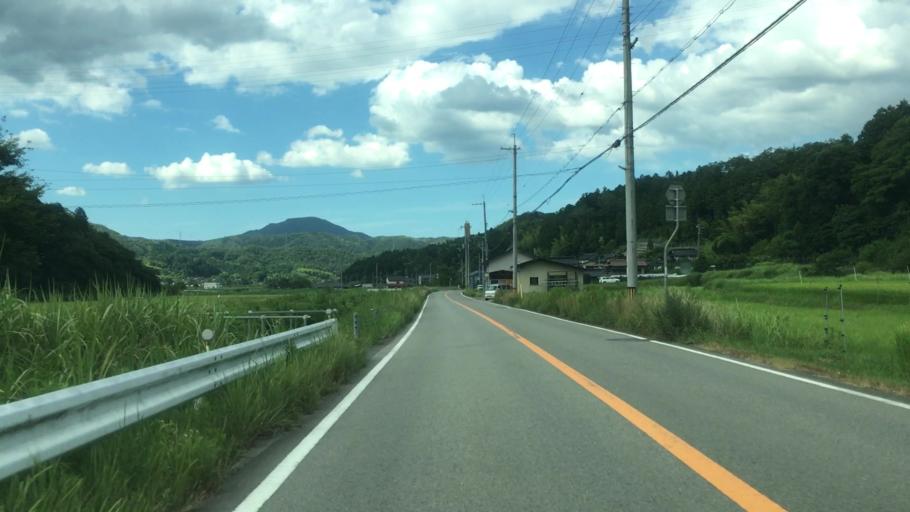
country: JP
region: Hyogo
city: Toyooka
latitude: 35.5375
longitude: 134.7899
